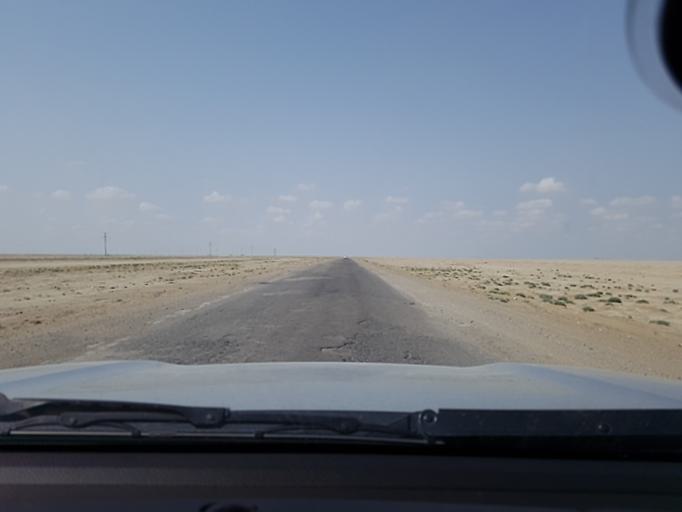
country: TM
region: Balkan
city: Gumdag
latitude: 38.6409
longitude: 54.3753
